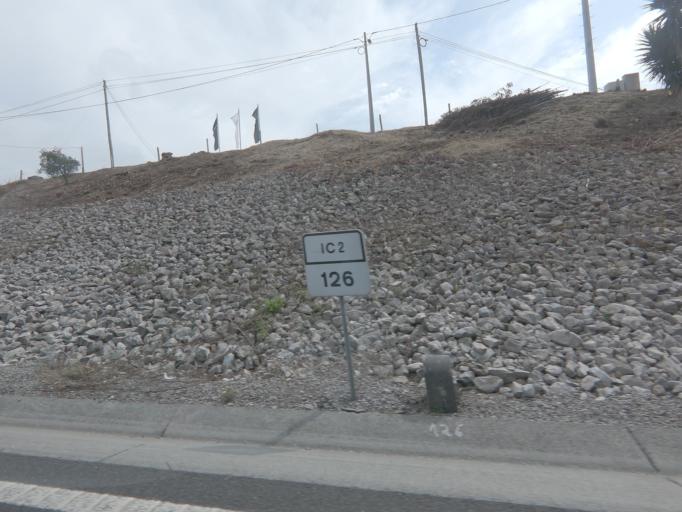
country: PT
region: Leiria
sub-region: Leiria
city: Leiria
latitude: 39.7628
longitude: -8.7915
